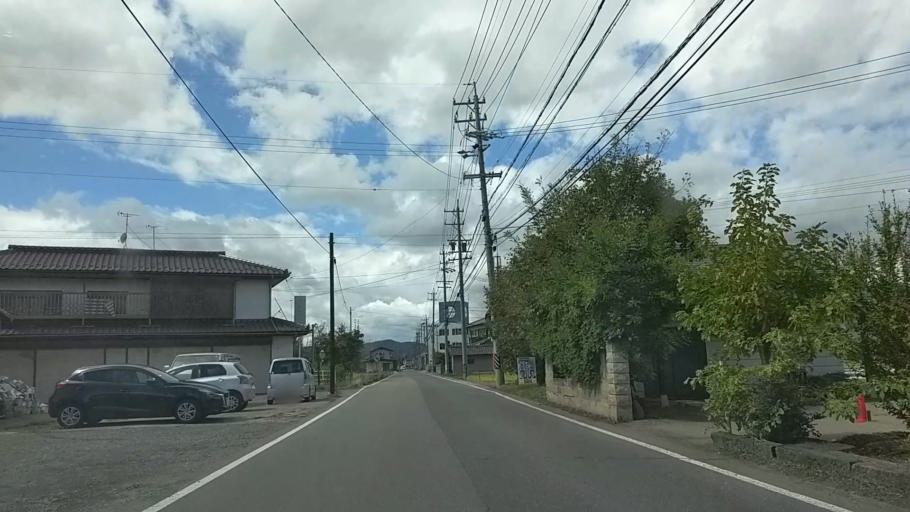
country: JP
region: Nagano
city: Nagano-shi
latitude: 36.6096
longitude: 138.2038
